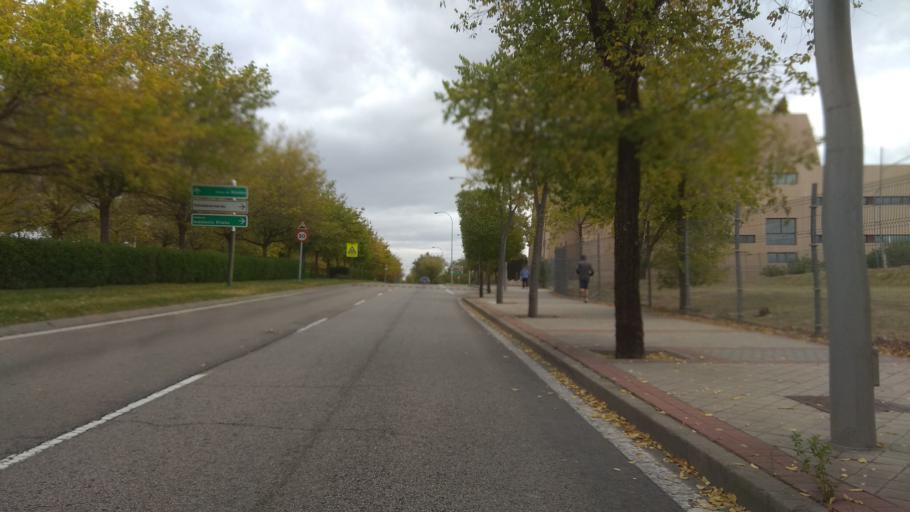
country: ES
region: Madrid
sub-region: Provincia de Madrid
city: Vicalvaro
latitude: 40.4058
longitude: -3.6210
